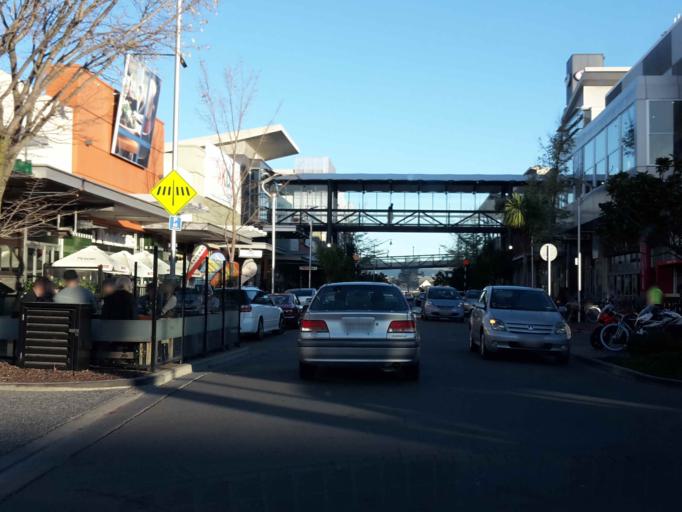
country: NZ
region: Canterbury
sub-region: Christchurch City
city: Christchurch
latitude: -43.5302
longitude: 172.6004
